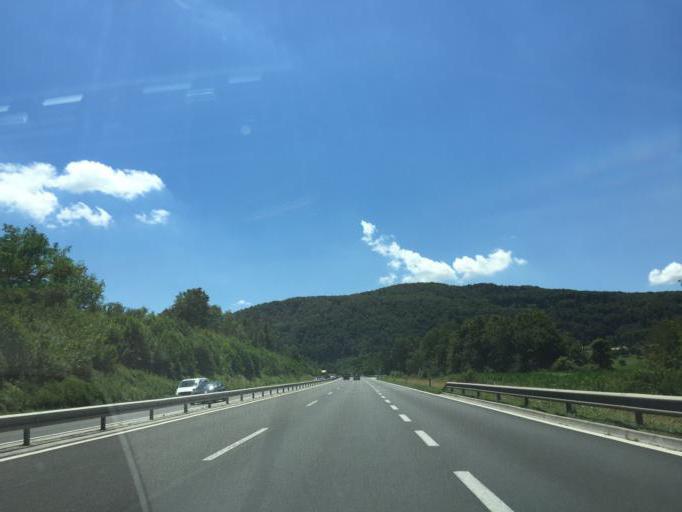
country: SI
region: Slovenska Konjice
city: Slovenske Konjice
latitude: 46.3257
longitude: 15.4645
